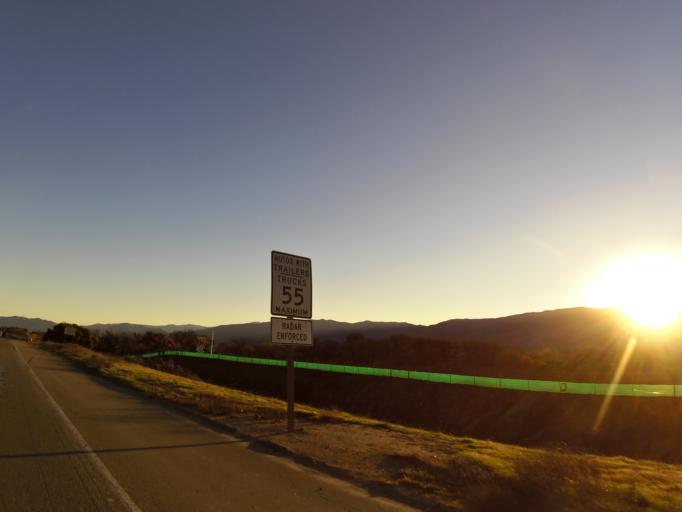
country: US
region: California
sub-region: Monterey County
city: Soledad
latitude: 36.4137
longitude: -121.3209
